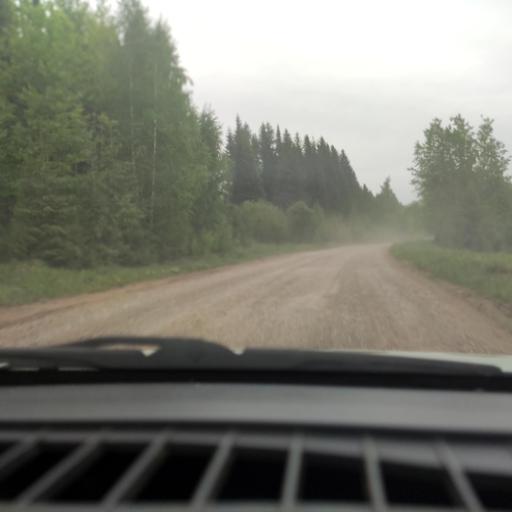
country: RU
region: Perm
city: Novyye Lyady
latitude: 57.9175
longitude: 56.6611
